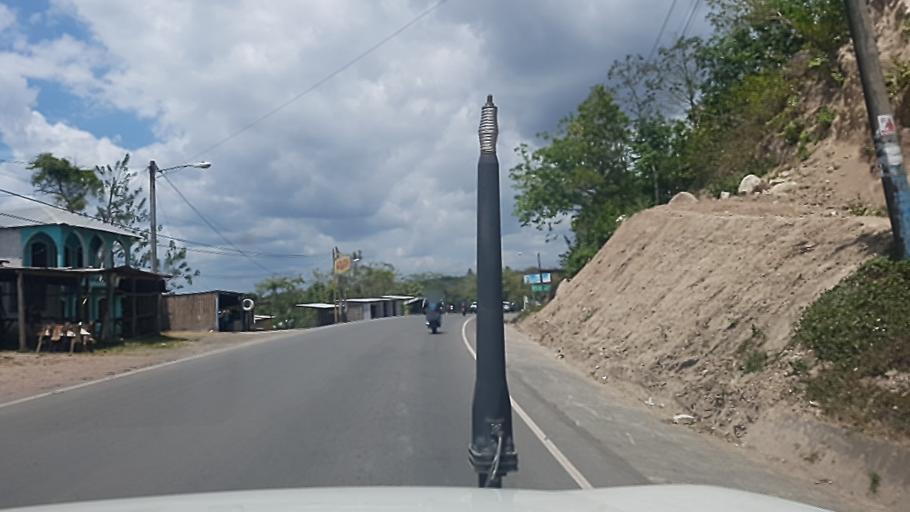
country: NI
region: Chontales
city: Santo Tomas
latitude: 12.0700
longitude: -85.0979
